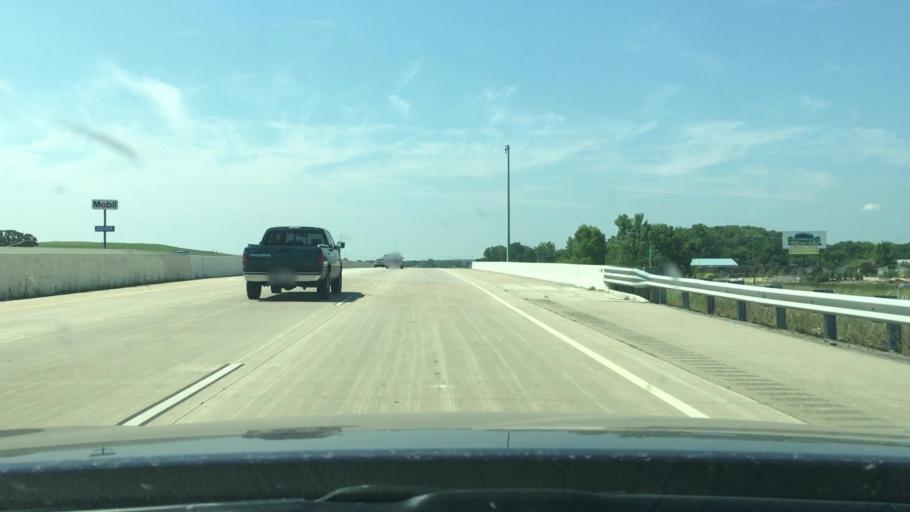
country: US
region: Wisconsin
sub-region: Winnebago County
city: Oshkosh
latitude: 44.0974
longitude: -88.5427
